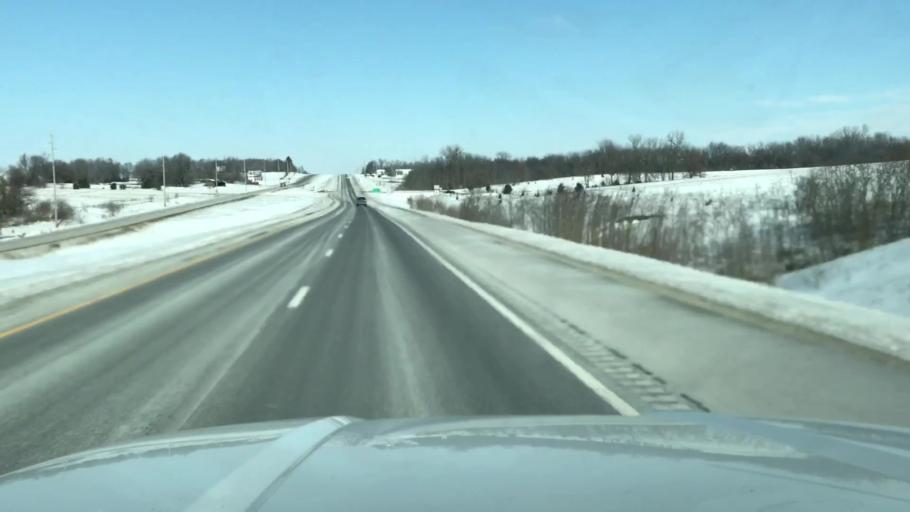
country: US
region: Missouri
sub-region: Nodaway County
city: Maryville
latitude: 40.1963
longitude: -94.8675
